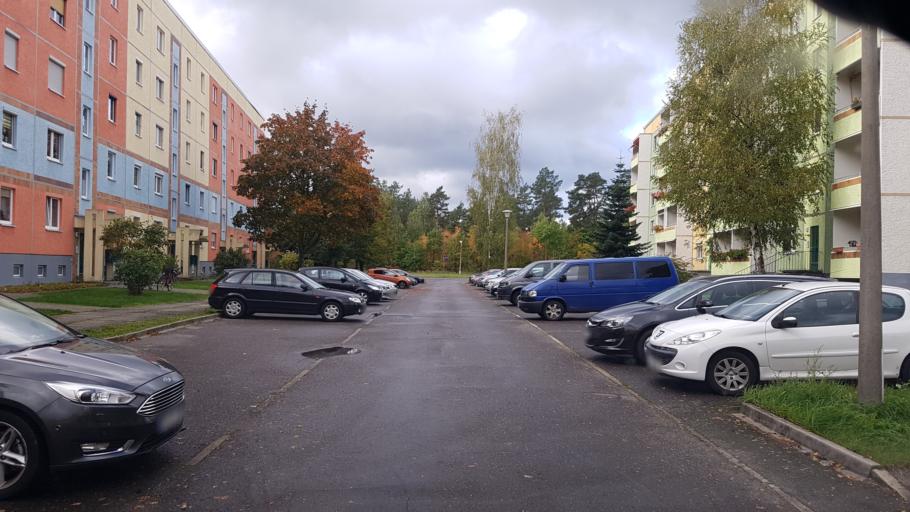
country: DE
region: Brandenburg
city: Grossraschen
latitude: 51.5970
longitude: 14.0000
